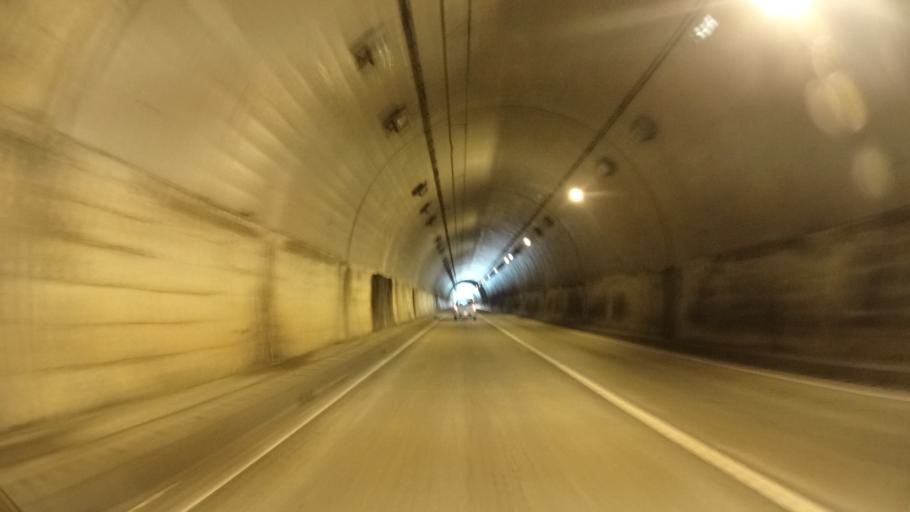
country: JP
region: Ehime
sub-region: Nishiuwa-gun
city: Ikata-cho
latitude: 33.4902
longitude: 132.3470
